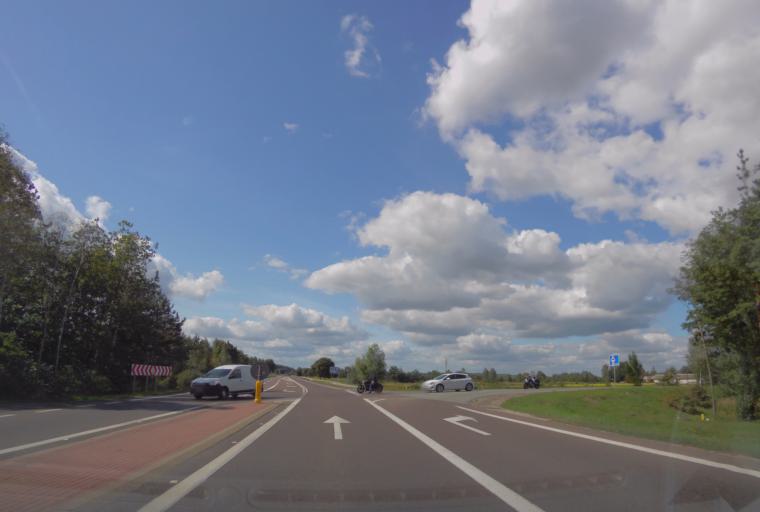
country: PL
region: Subcarpathian Voivodeship
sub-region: Tarnobrzeg
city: Tarnobrzeg
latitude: 50.4865
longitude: 21.6829
